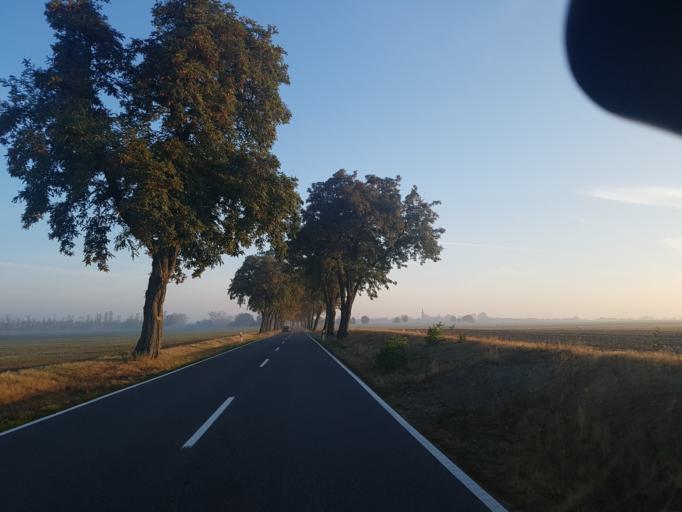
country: DE
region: Brandenburg
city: Juterbog
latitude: 51.9105
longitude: 13.0809
